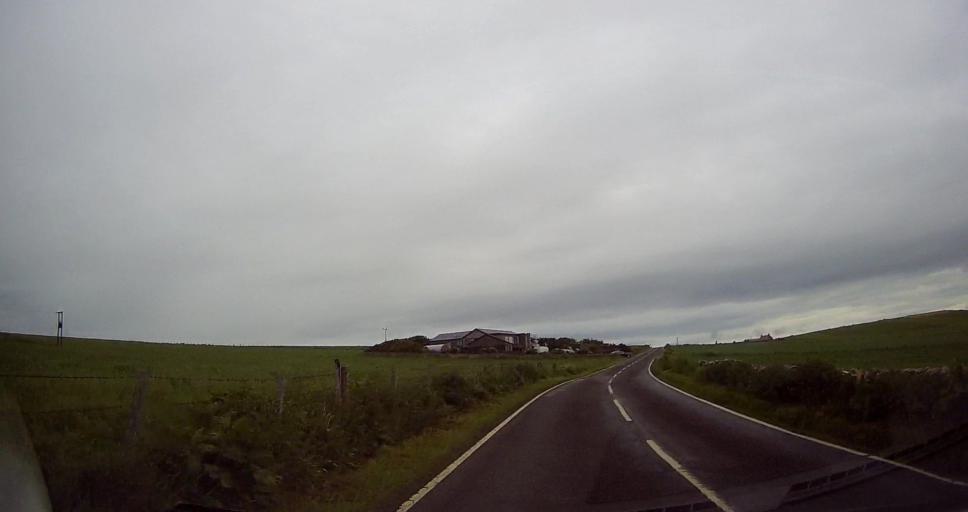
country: GB
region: Scotland
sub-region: Orkney Islands
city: Stromness
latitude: 59.0180
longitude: -3.3046
